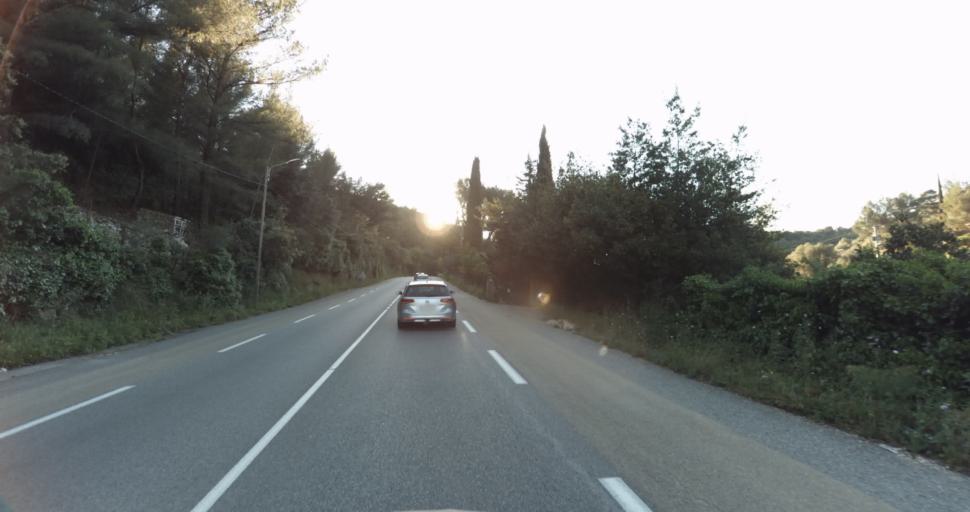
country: FR
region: Provence-Alpes-Cote d'Azur
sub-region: Departement du Var
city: La Valette-du-Var
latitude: 43.1524
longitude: 5.9667
